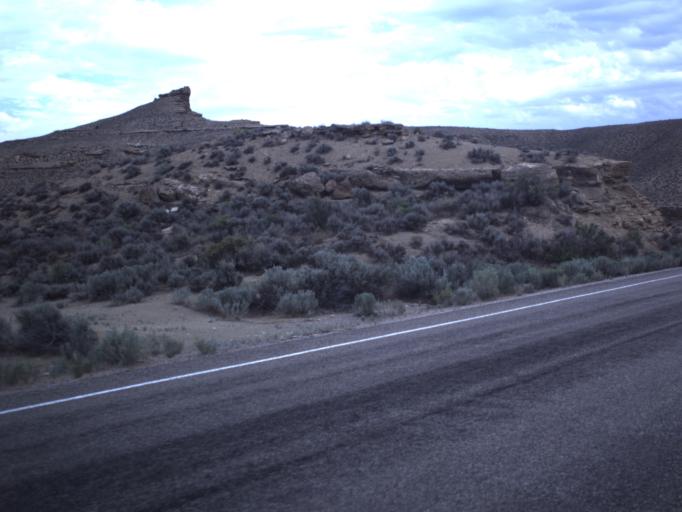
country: US
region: Colorado
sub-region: Rio Blanco County
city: Rangely
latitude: 39.9914
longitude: -109.1775
